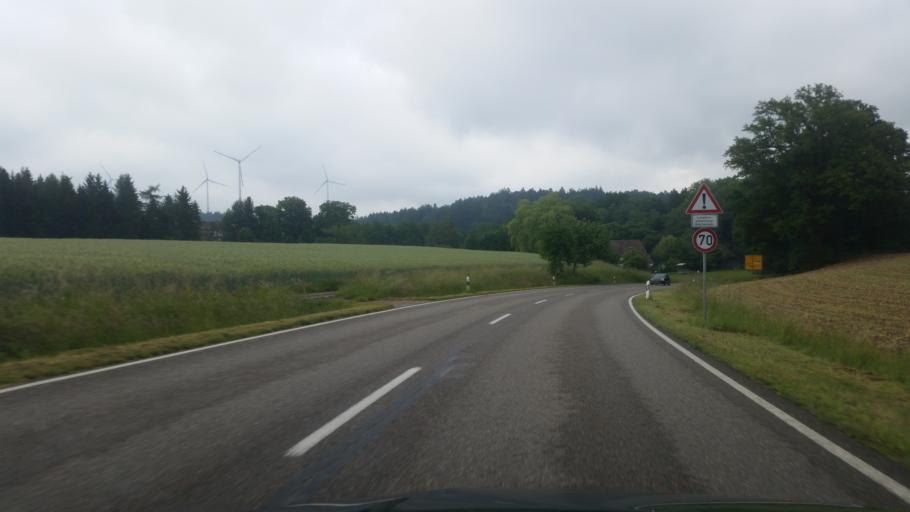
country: DE
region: Baden-Wuerttemberg
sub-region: Regierungsbezirk Stuttgart
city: Rosenberg
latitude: 49.0260
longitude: 9.9882
